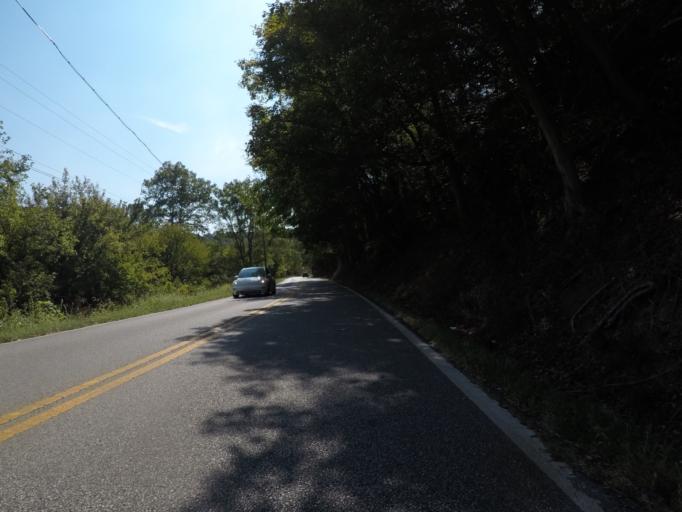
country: US
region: West Virginia
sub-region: Cabell County
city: Lesage
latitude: 38.5221
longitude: -82.3890
